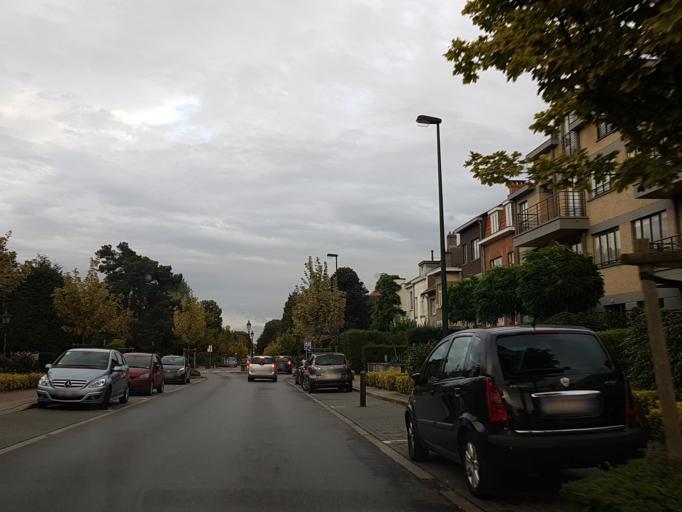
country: BE
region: Flanders
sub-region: Provincie Vlaams-Brabant
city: Kraainem
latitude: 50.8337
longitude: 4.4480
